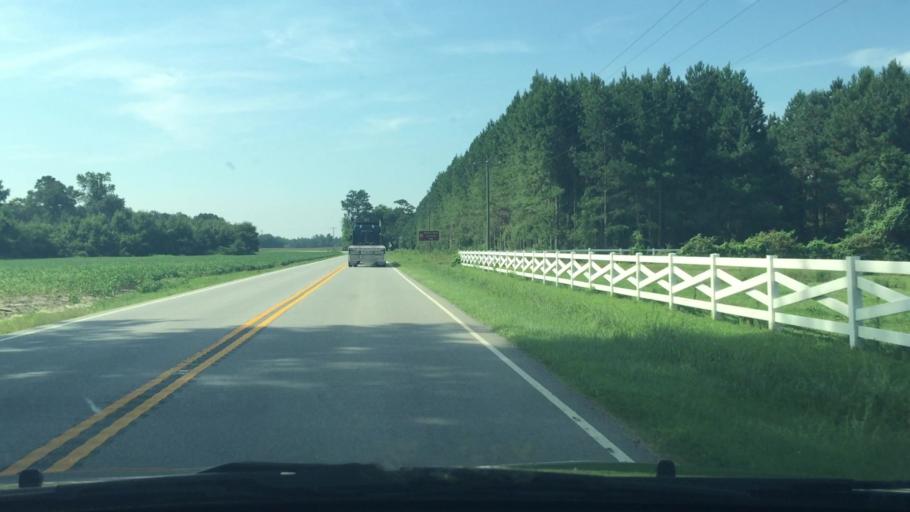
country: US
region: Virginia
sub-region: Sussex County
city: Sussex
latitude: 36.8886
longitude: -77.1540
